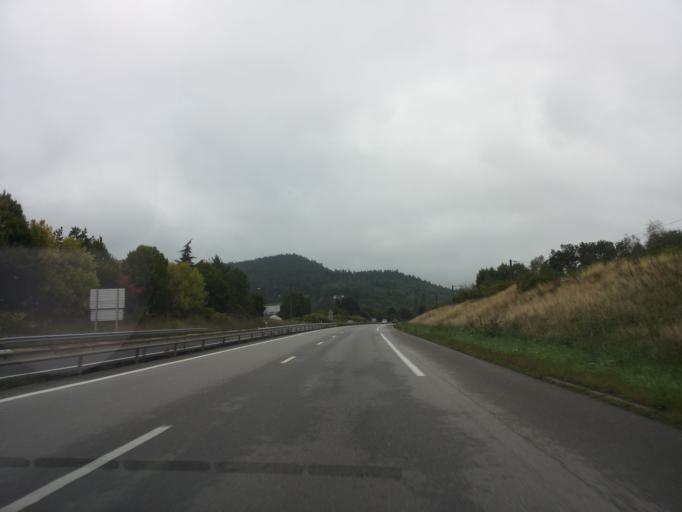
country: FR
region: Lorraine
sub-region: Departement des Vosges
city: Saint-Nabord
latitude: 48.0491
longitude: 6.5825
